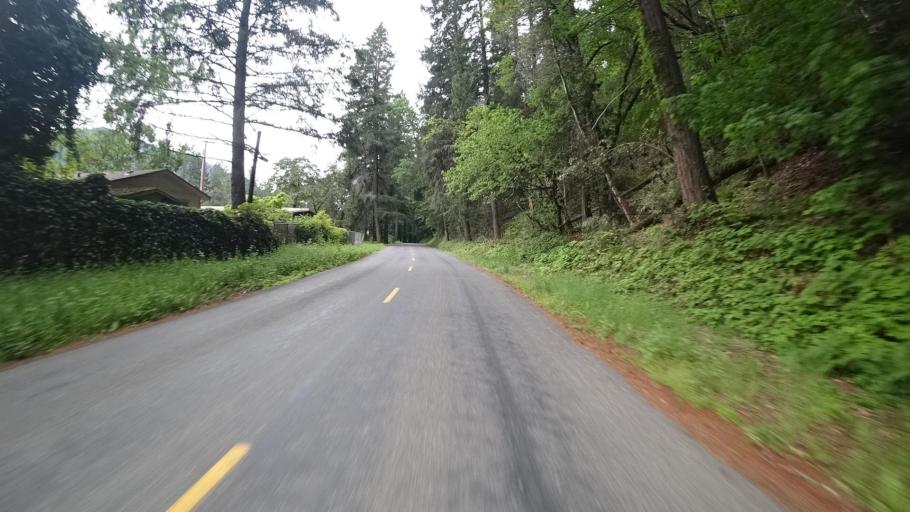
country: US
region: California
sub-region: Humboldt County
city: Willow Creek
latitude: 40.9536
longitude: -123.6301
